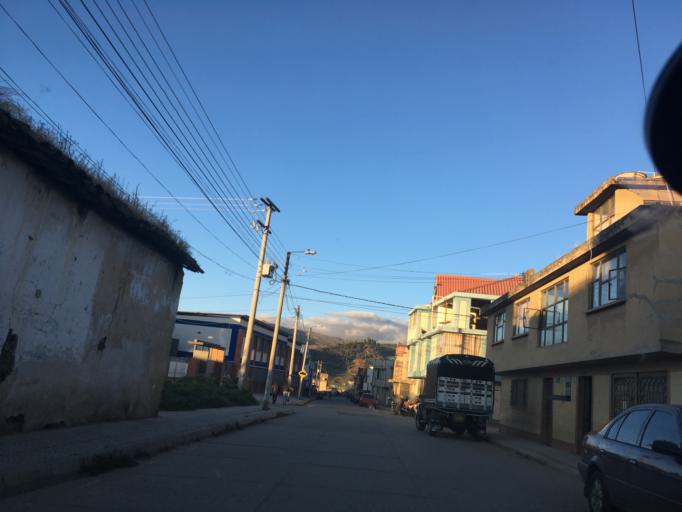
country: CO
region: Boyaca
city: Aquitania
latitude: 5.5199
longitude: -72.8835
